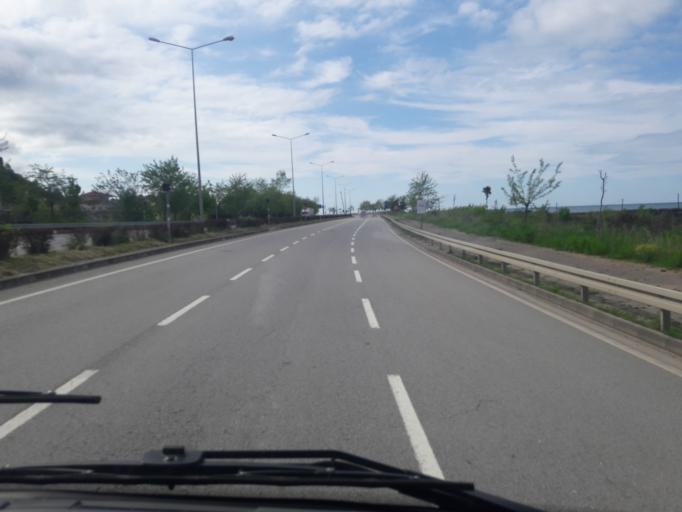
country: TR
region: Giresun
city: Piraziz
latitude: 40.9550
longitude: 38.1207
